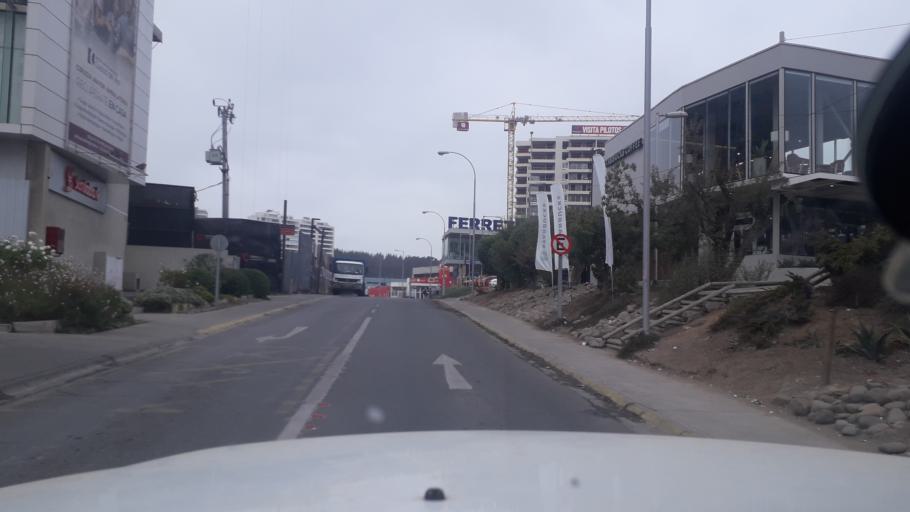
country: CL
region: Valparaiso
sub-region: Provincia de Valparaiso
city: Vina del Mar
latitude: -32.9568
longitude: -71.5441
